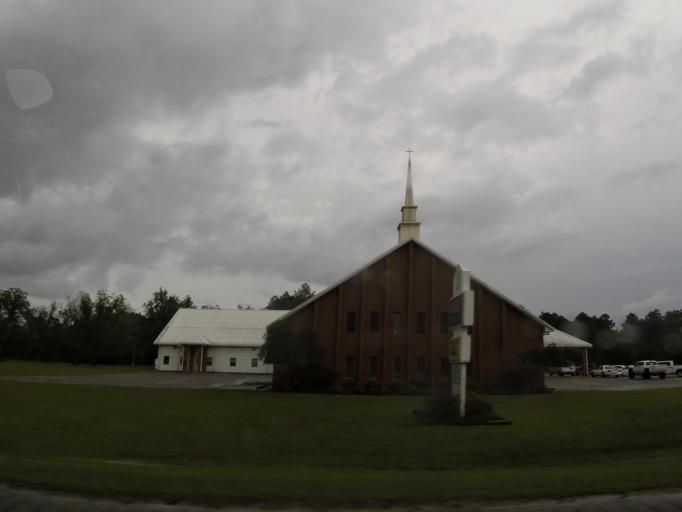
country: US
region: Georgia
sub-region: Wayne County
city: Jesup
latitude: 31.5793
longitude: -81.8515
